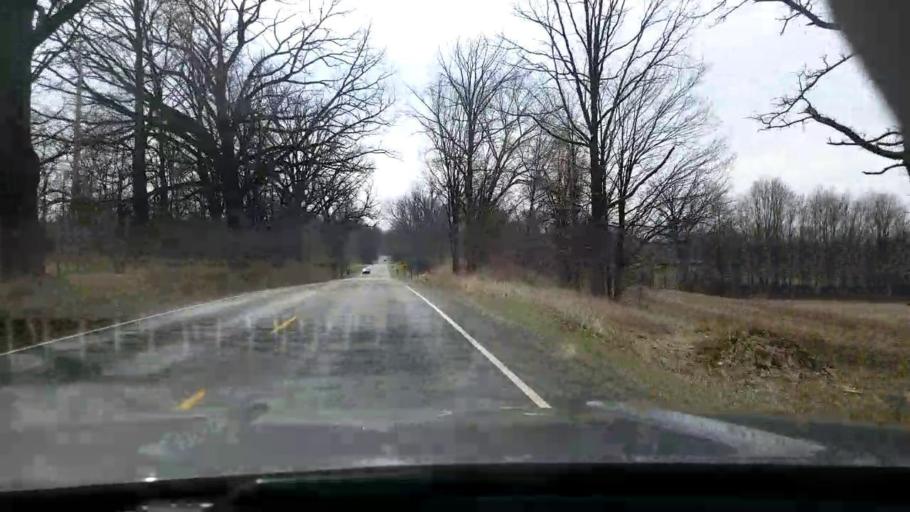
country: US
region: Michigan
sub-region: Jackson County
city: Spring Arbor
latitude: 42.1820
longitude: -84.5204
